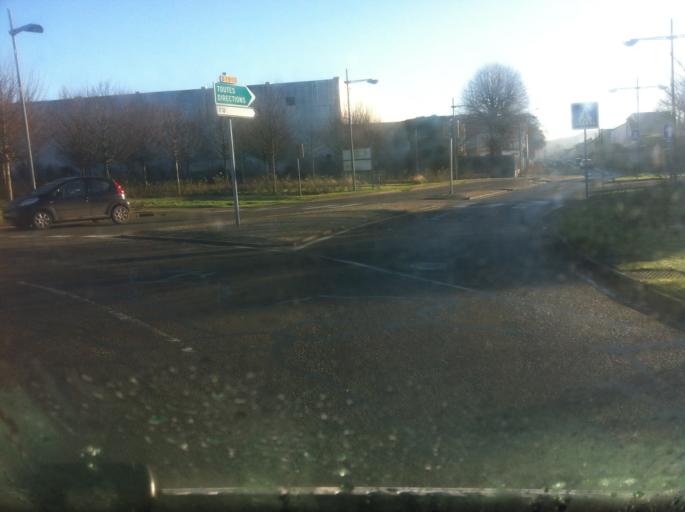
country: FR
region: Picardie
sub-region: Departement de la Somme
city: Mers-les-Bains
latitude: 50.0563
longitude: 1.3869
